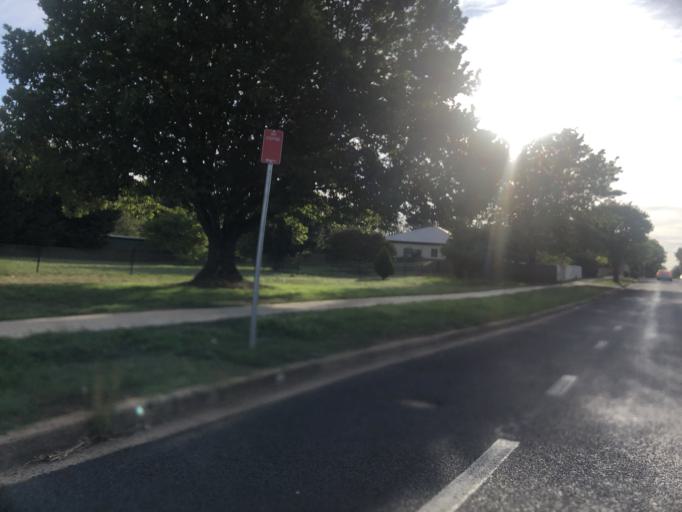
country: AU
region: New South Wales
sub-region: Orange Municipality
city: Orange
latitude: -33.2937
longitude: 149.0935
